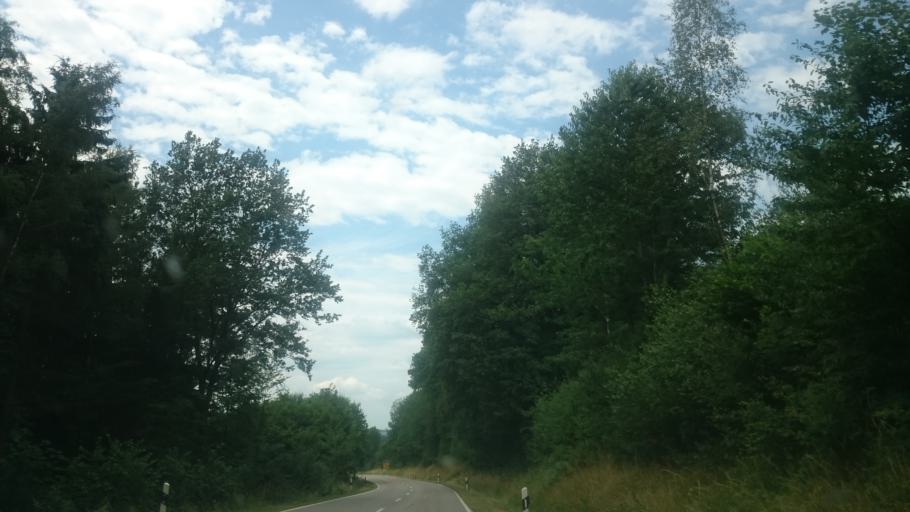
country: DE
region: Bavaria
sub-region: Lower Bavaria
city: Perasdorf
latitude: 48.9722
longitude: 12.7845
